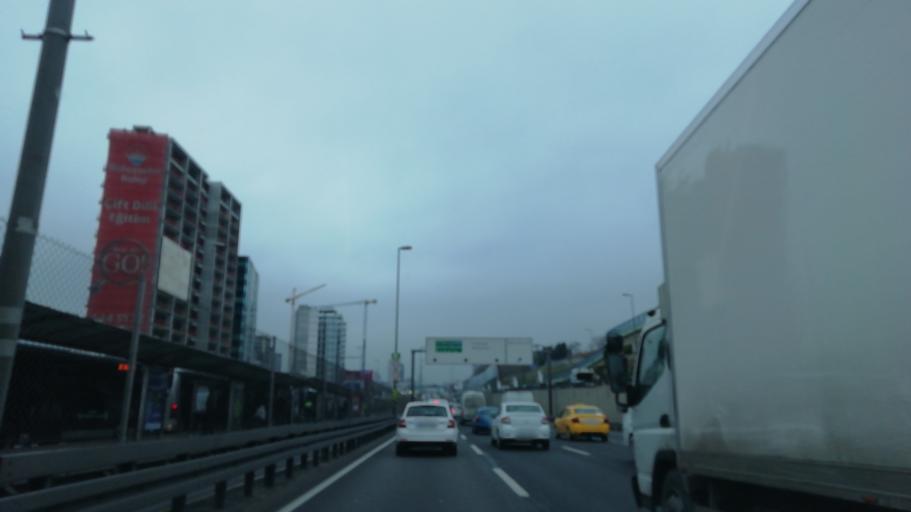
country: TR
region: Istanbul
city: guengoeren merter
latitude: 41.0076
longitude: 28.8975
